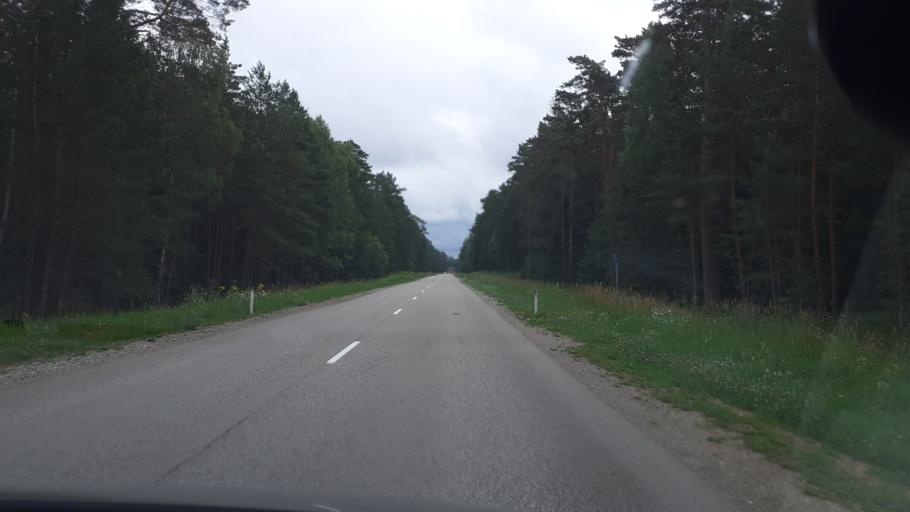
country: LV
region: Ventspils Rajons
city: Piltene
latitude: 57.1118
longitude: 21.7612
